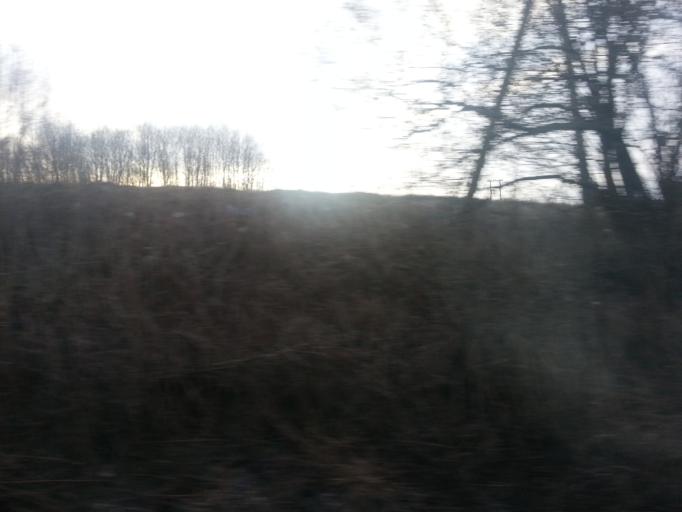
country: NO
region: Sor-Trondelag
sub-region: Melhus
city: Melhus
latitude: 63.3346
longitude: 10.3435
